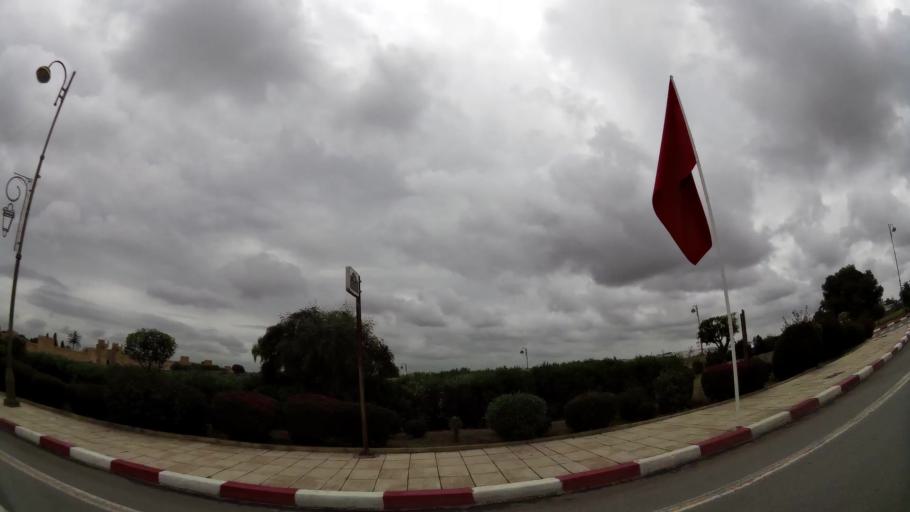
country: MA
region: Rabat-Sale-Zemmour-Zaer
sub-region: Rabat
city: Rabat
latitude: 34.0068
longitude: -6.8258
